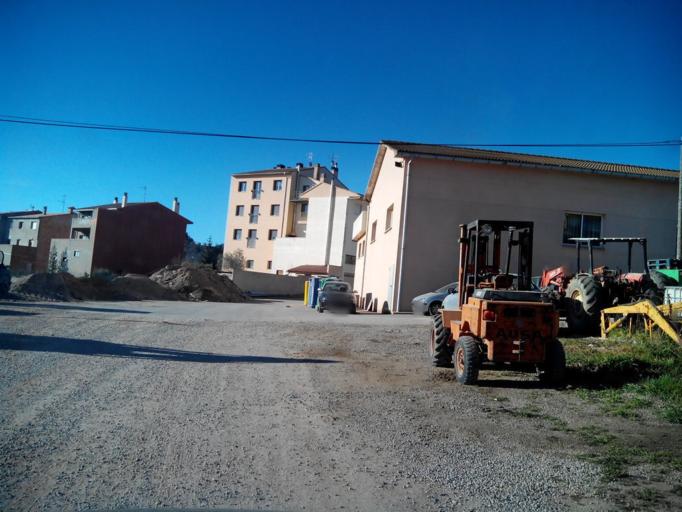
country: ES
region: Catalonia
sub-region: Provincia de Barcelona
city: Capolat
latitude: 42.0181
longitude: 1.7360
